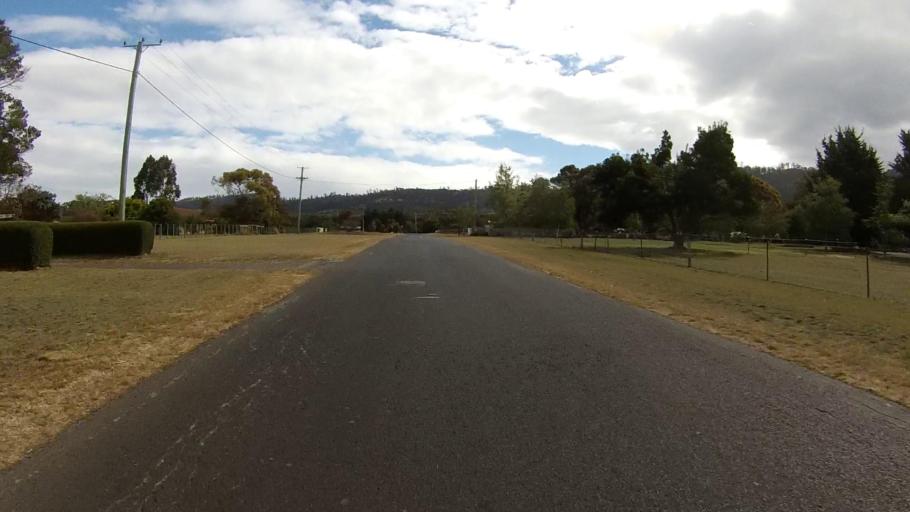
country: AU
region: Tasmania
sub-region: Clarence
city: Acton Park
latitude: -42.8649
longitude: 147.4847
